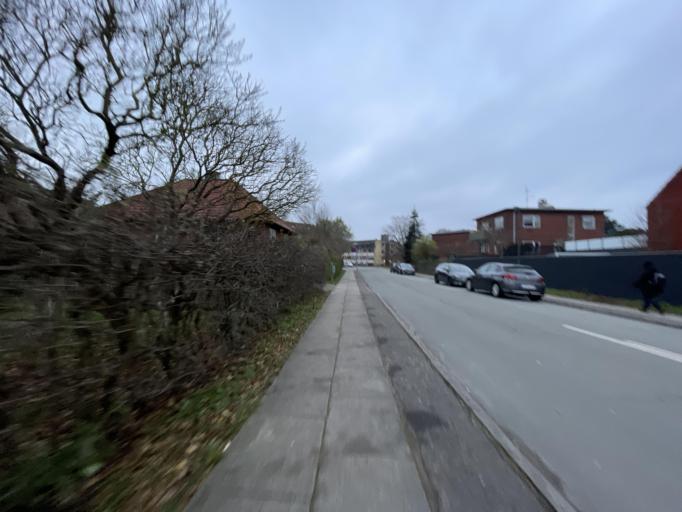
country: DK
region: Capital Region
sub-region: Kobenhavn
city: Vanlose
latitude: 55.6900
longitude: 12.4925
